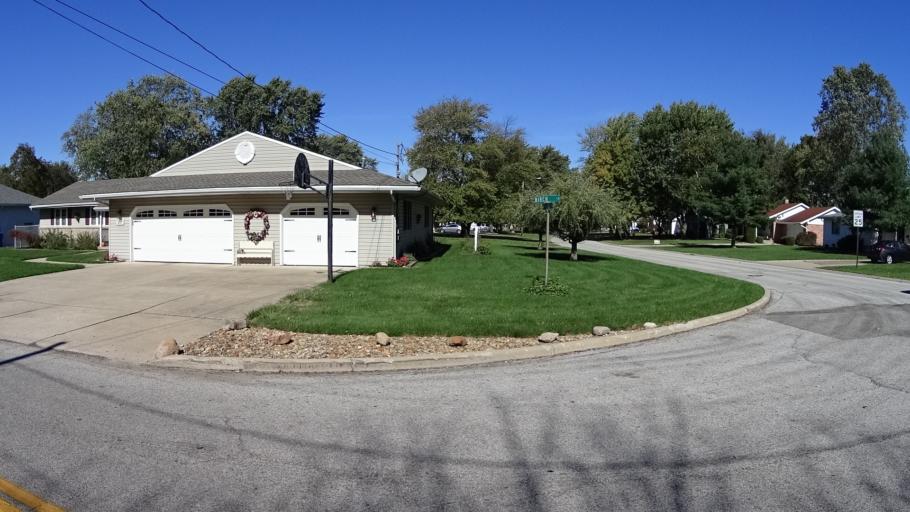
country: US
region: Ohio
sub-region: Lorain County
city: Amherst
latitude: 41.4045
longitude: -82.2159
